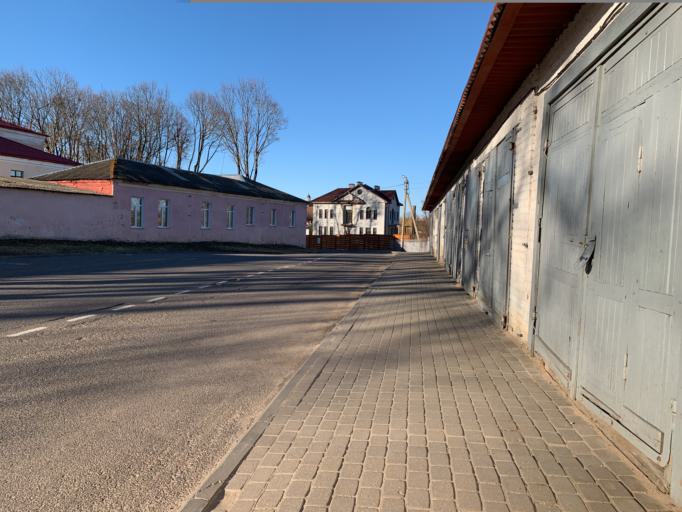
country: BY
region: Minsk
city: Nyasvizh
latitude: 53.2154
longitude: 26.6823
